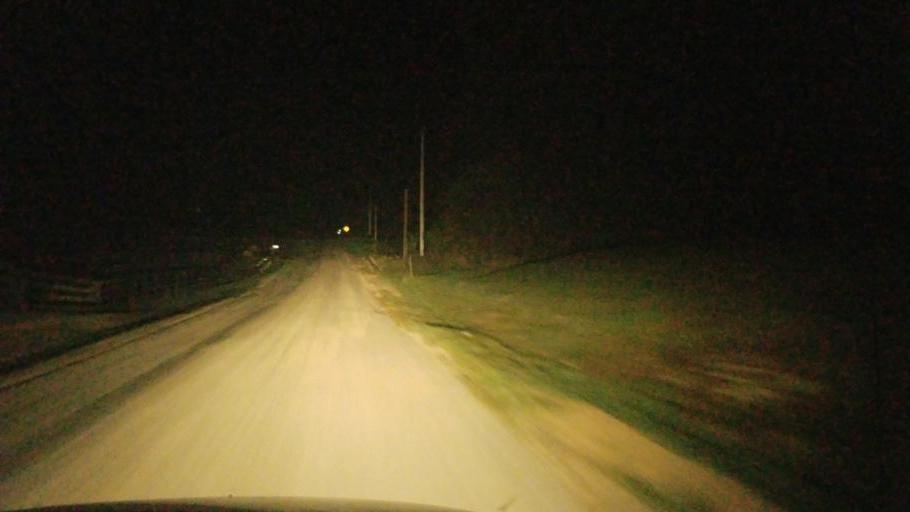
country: US
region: Ohio
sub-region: Highland County
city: Leesburg
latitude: 39.2990
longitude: -83.5545
